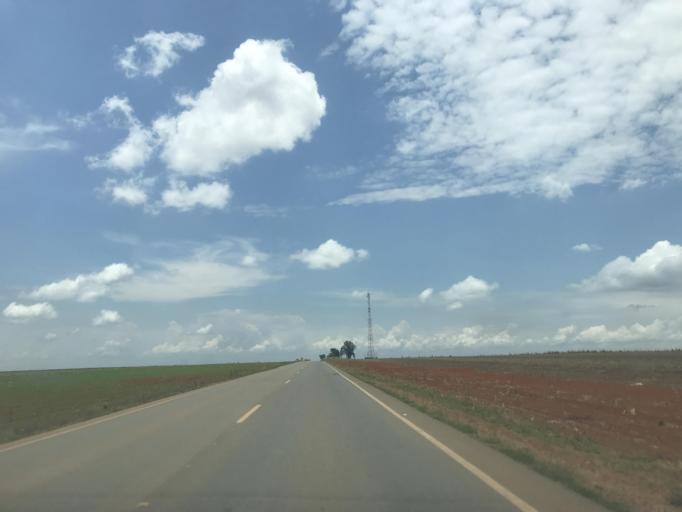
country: BR
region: Goias
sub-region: Vianopolis
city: Vianopolis
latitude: -16.5322
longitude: -48.2476
